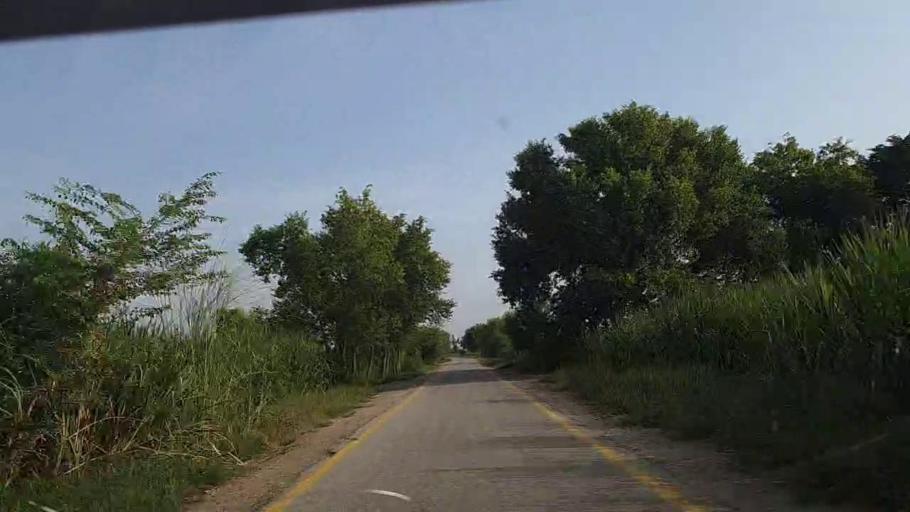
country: PK
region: Sindh
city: Adilpur
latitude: 27.9680
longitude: 69.2560
